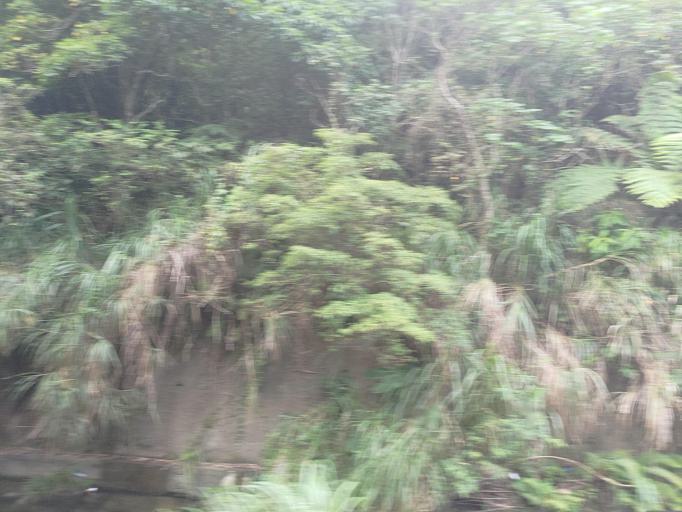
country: TW
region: Taiwan
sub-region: Hsinchu
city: Hsinchu
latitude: 24.6110
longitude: 121.0407
